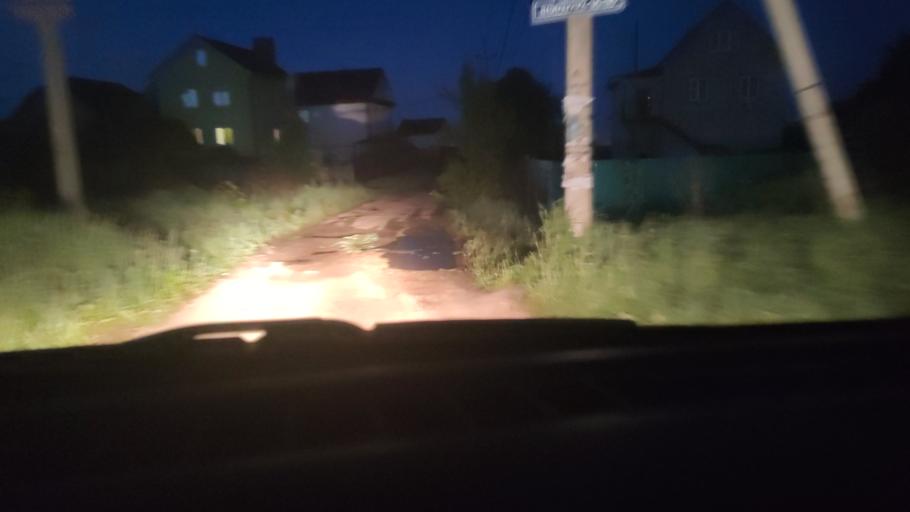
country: RU
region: Perm
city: Froly
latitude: 57.9280
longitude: 56.2743
